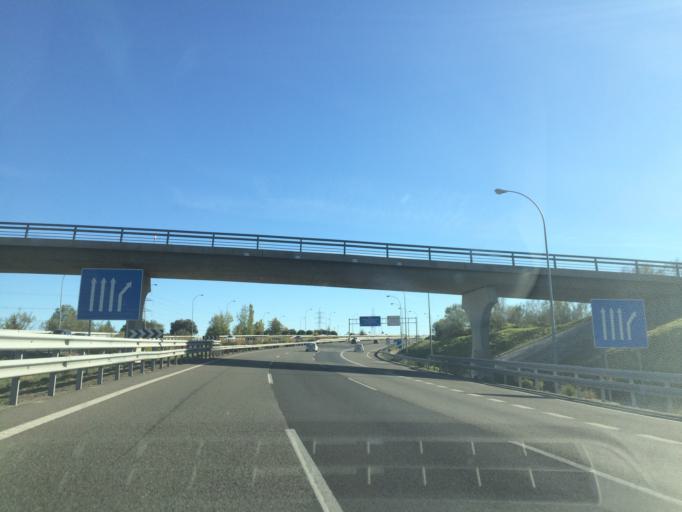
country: ES
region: Madrid
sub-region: Provincia de Madrid
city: Pozuelo de Alarcon
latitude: 40.4153
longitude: -3.8226
